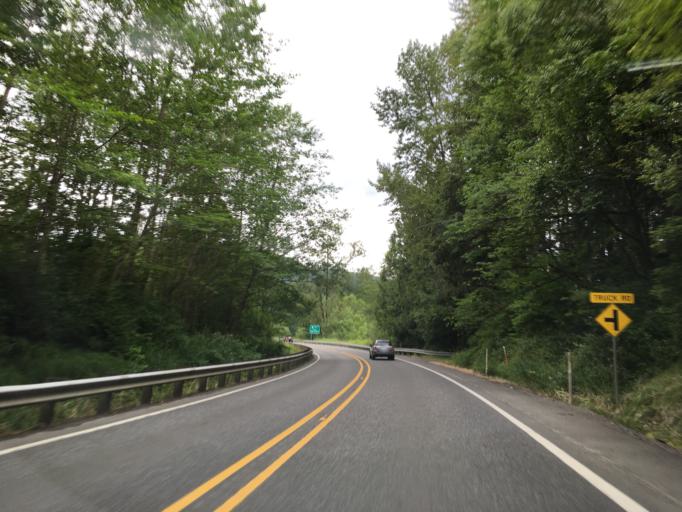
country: US
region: Washington
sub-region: Whatcom County
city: Peaceful Valley
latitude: 48.8214
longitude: -122.1938
